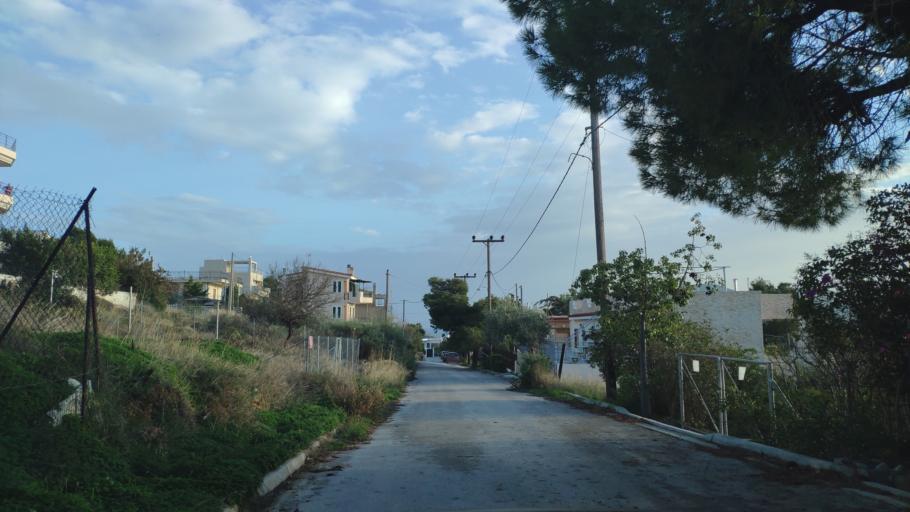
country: GR
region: Attica
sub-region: Nomarchia Anatolikis Attikis
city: Limin Mesoyaias
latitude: 37.9000
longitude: 24.0287
